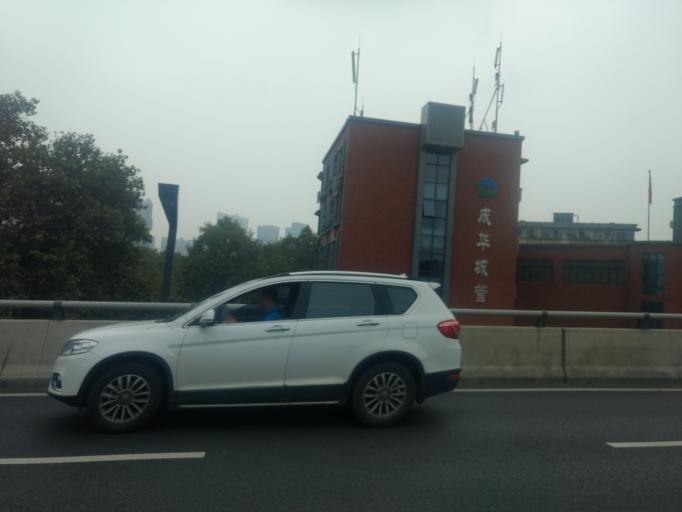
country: CN
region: Sichuan
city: Chengdu
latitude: 30.6822
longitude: 104.0949
